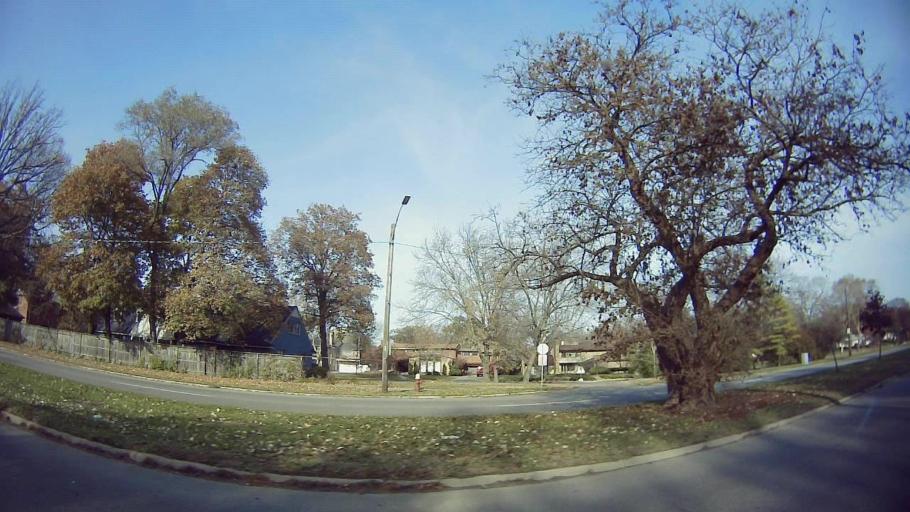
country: US
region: Michigan
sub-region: Oakland County
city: Ferndale
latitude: 42.4319
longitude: -83.1214
